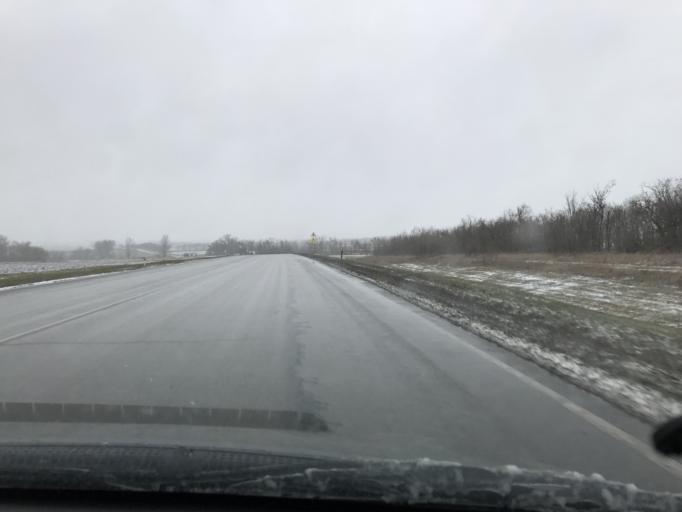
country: RU
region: Rostov
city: Mechetinskaya
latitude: 46.6756
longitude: 40.5270
